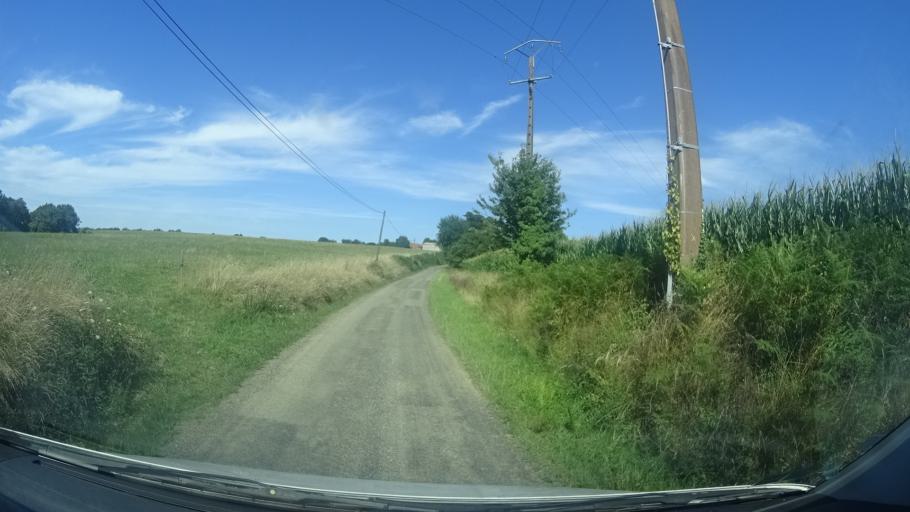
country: FR
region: Aquitaine
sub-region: Departement des Pyrenees-Atlantiques
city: Orthez
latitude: 43.5055
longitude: -0.7117
